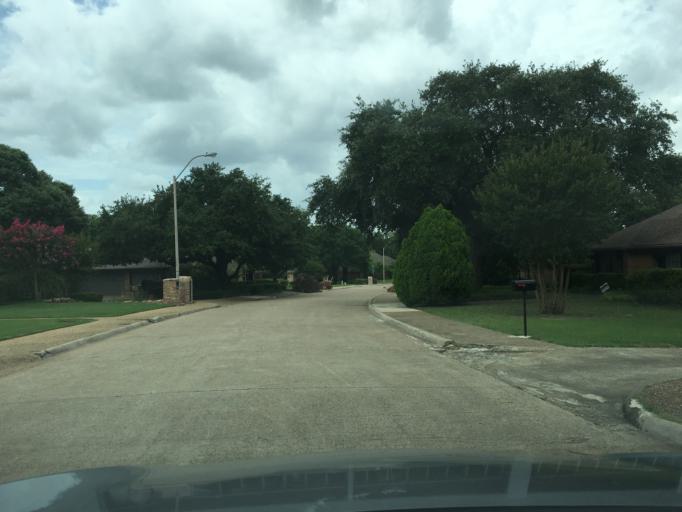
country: US
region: Texas
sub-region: Dallas County
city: Richardson
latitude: 32.9125
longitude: -96.7138
